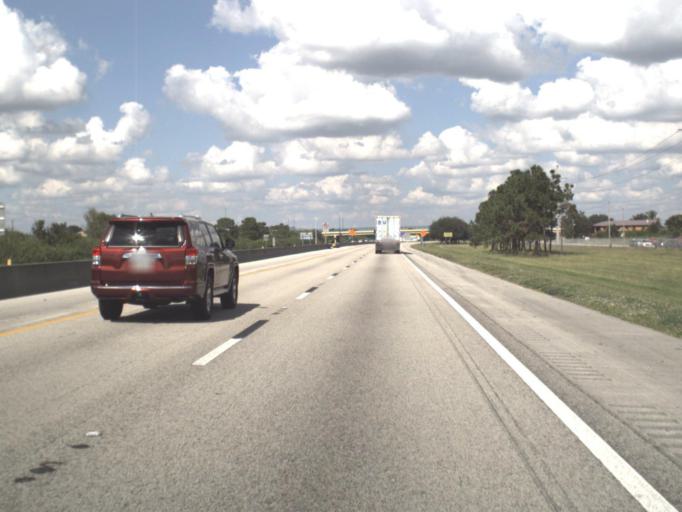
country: US
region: Florida
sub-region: Saint Lucie County
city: Port Saint Lucie
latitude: 27.2900
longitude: -80.3676
